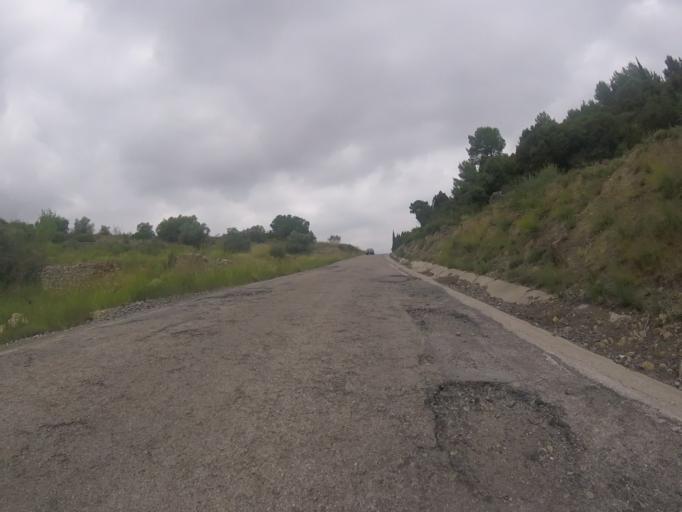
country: ES
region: Valencia
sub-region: Provincia de Castello
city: Cabanes
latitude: 40.1216
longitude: 0.0453
